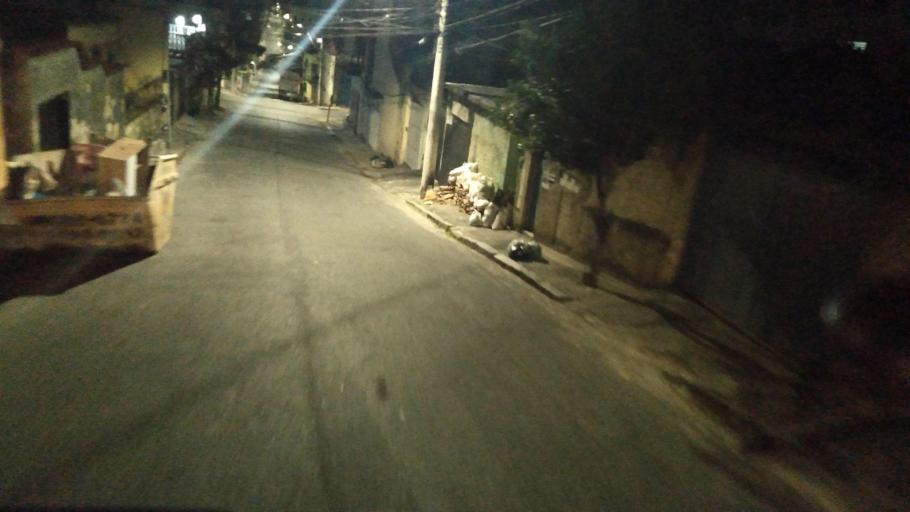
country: BR
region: Minas Gerais
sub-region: Belo Horizonte
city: Belo Horizonte
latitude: -19.8882
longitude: -43.9620
